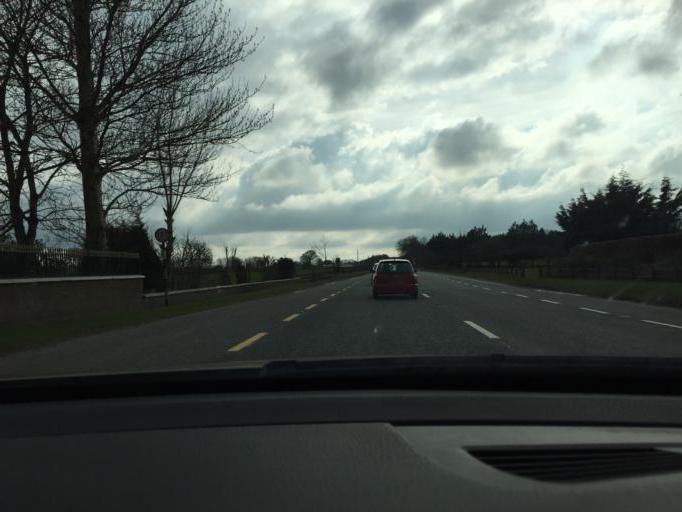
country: IE
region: Leinster
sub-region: Wicklow
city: Blessington
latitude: 53.1908
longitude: -6.5130
